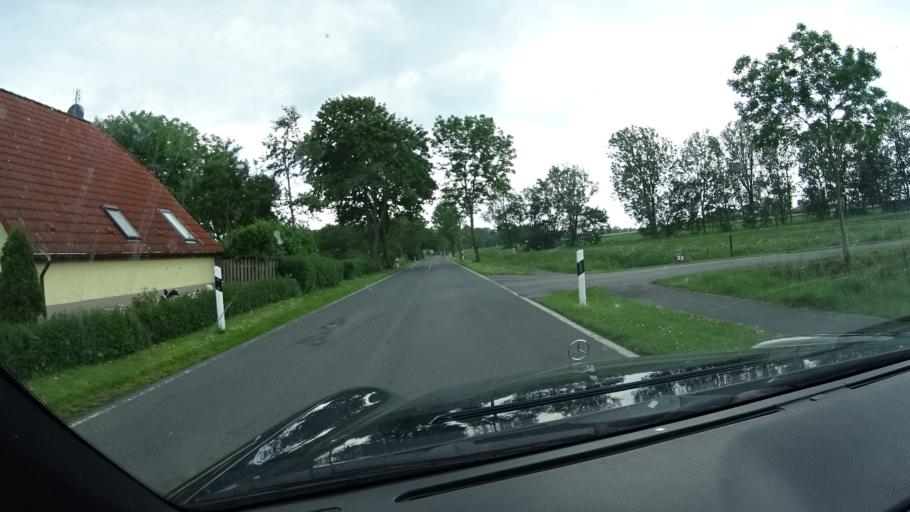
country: DE
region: Lower Saxony
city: Butjadingen
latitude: 53.5852
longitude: 8.2716
